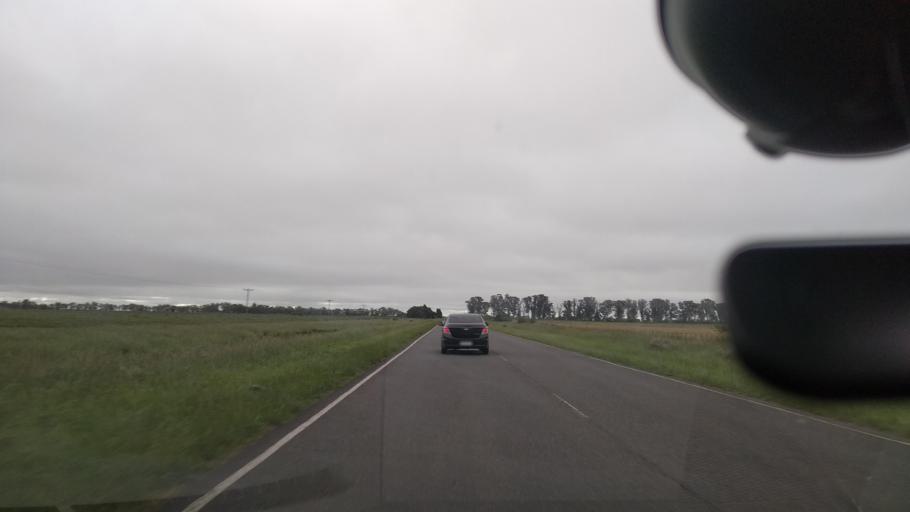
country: AR
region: Buenos Aires
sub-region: Partido de Magdalena
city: Magdalena
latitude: -35.1967
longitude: -57.7846
